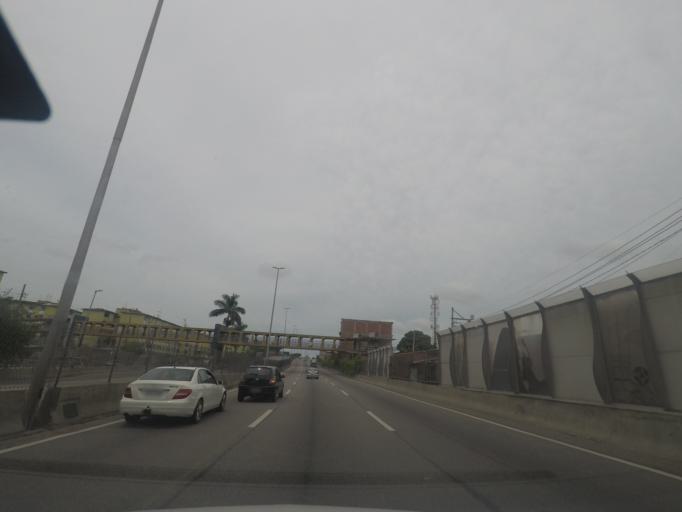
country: BR
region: Rio de Janeiro
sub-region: Sao Joao De Meriti
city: Sao Joao de Meriti
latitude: -22.9509
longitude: -43.3569
